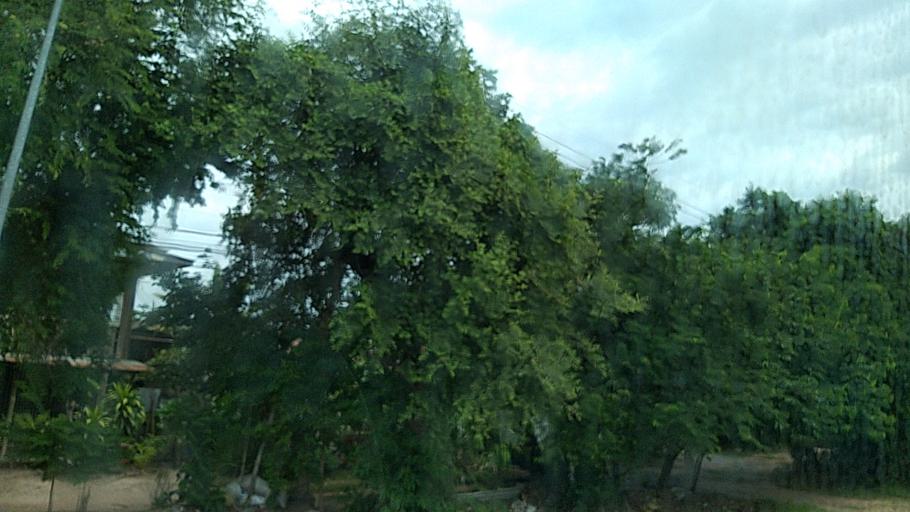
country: TH
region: Maha Sarakham
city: Maha Sarakham
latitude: 16.1564
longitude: 103.3696
